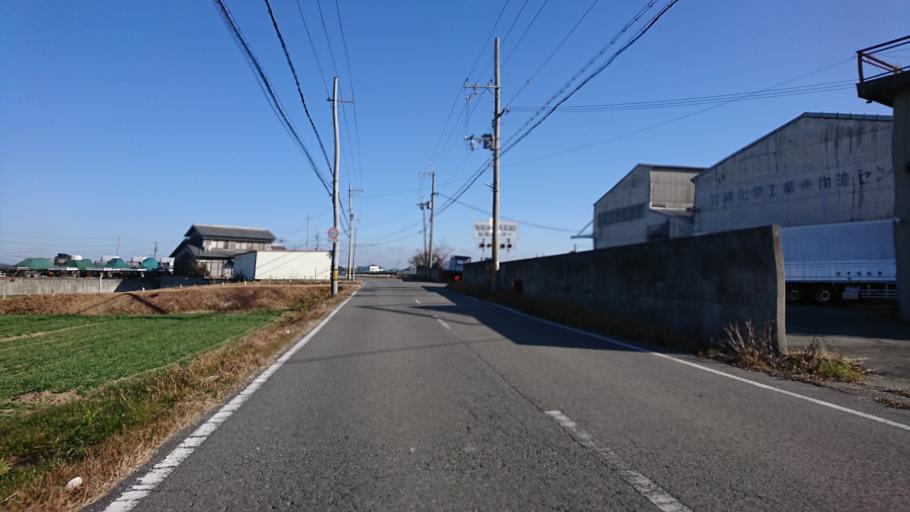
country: JP
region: Hyogo
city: Kakogawacho-honmachi
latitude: 34.7602
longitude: 134.9011
